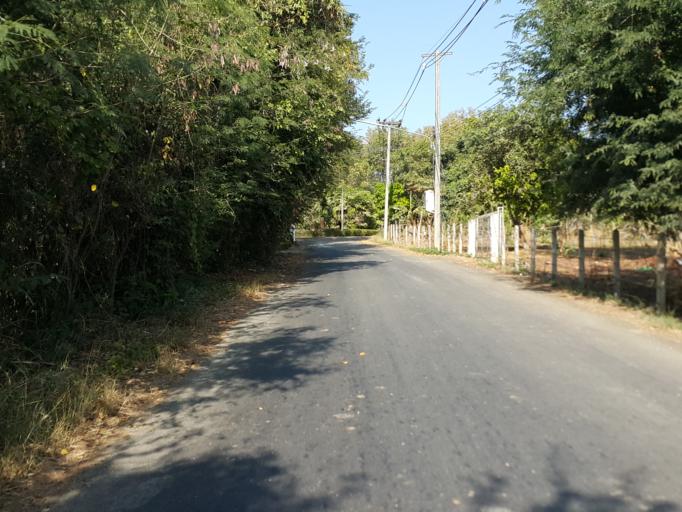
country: TH
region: Chiang Mai
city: Mae On
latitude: 18.8345
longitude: 99.2081
